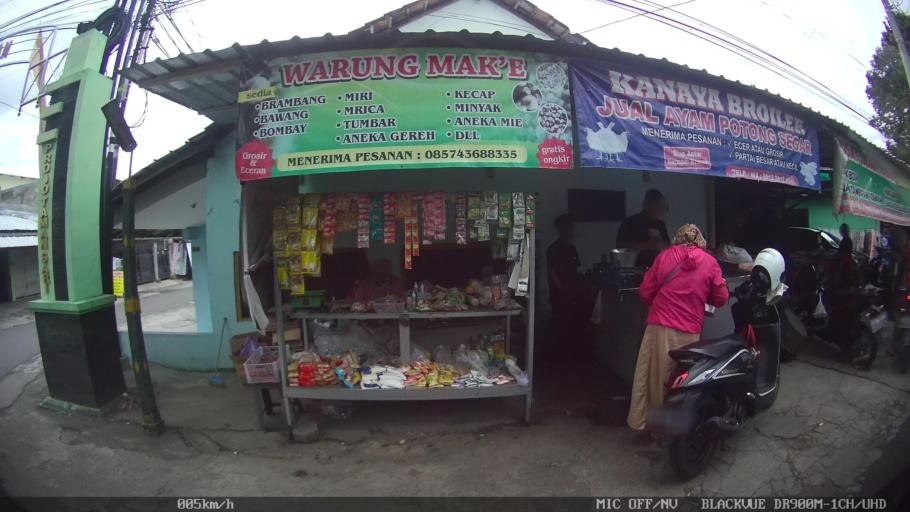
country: ID
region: Daerah Istimewa Yogyakarta
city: Depok
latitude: -7.8028
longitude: 110.4161
